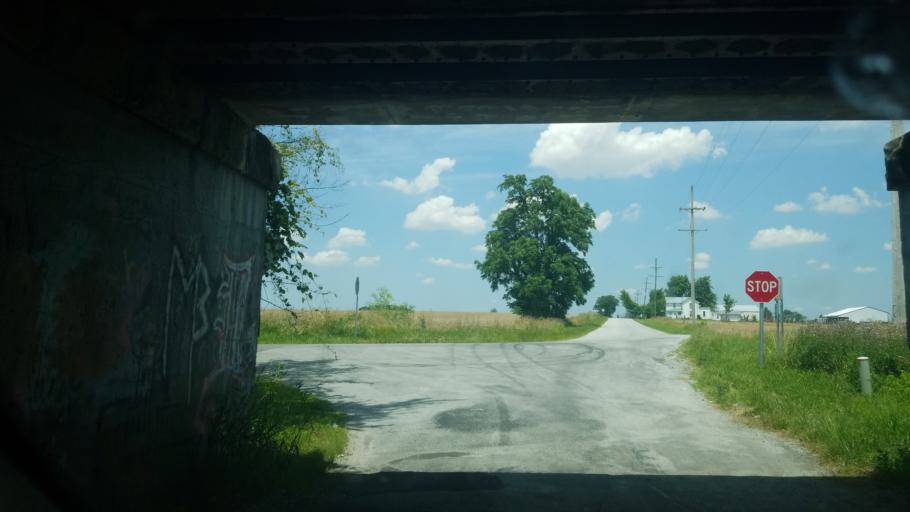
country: US
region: Ohio
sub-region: Hancock County
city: Arlington
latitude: 40.7899
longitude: -83.6331
